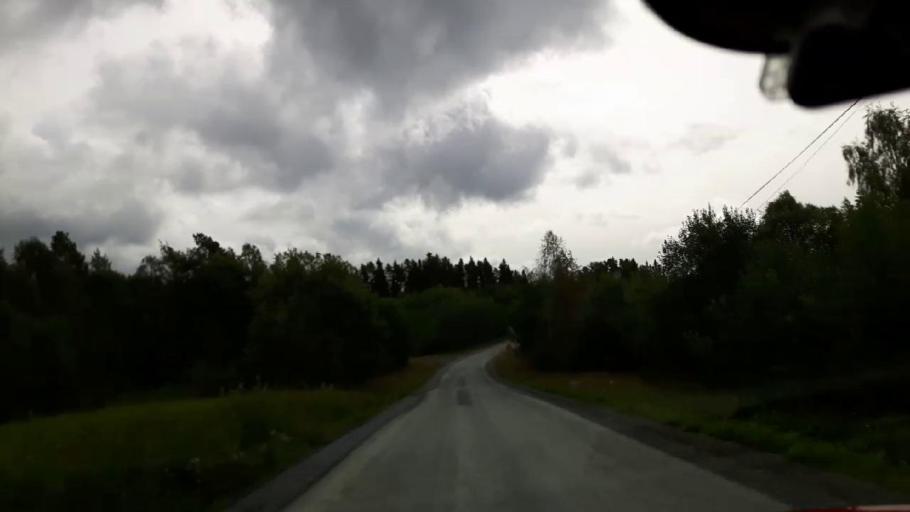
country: SE
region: Jaemtland
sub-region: Krokoms Kommun
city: Krokom
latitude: 63.5716
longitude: 14.2404
